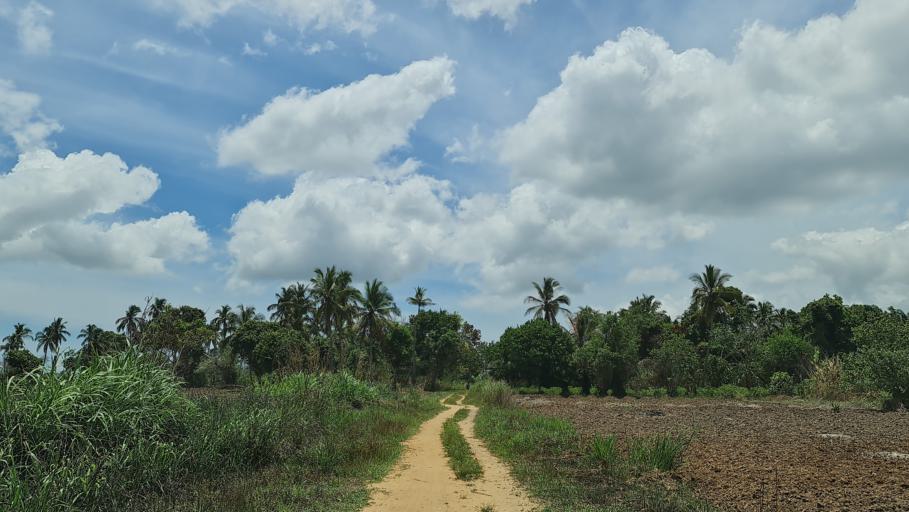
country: MZ
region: Zambezia
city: Quelimane
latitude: -17.5778
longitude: 37.3744
